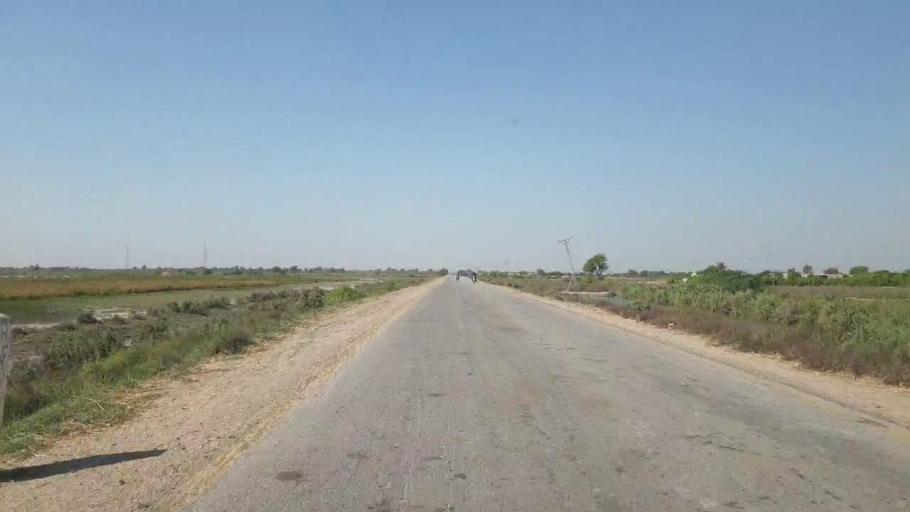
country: PK
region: Sindh
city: Rajo Khanani
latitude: 25.0533
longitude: 68.8058
